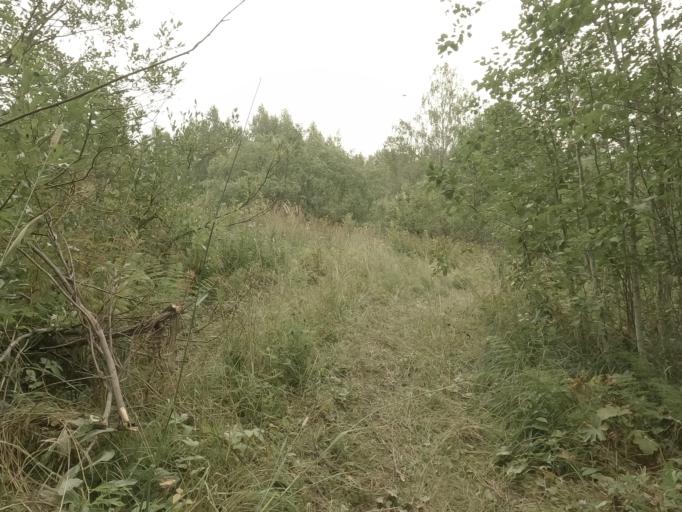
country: RU
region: Leningrad
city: Kamennogorsk
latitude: 61.0775
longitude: 29.1565
